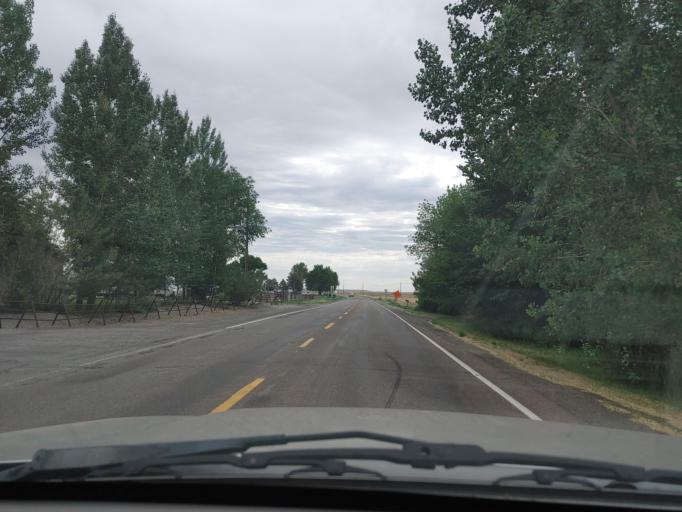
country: US
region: Idaho
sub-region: Lincoln County
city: Shoshone
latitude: 43.0493
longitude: -114.1513
